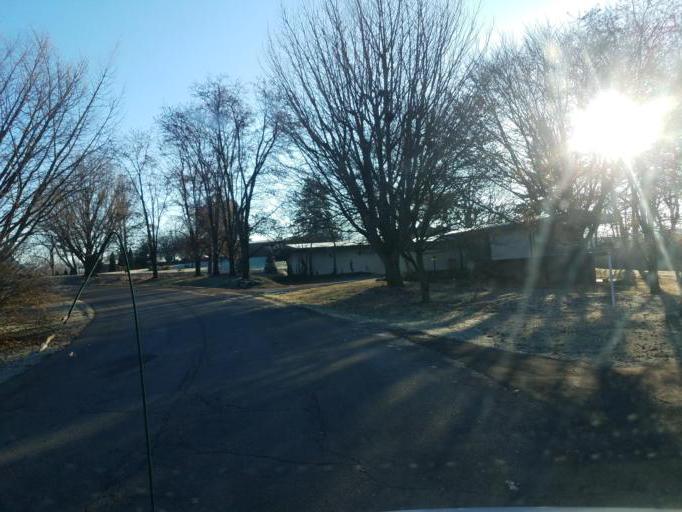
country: US
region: Ohio
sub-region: Marion County
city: Marion
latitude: 40.5718
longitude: -83.1159
